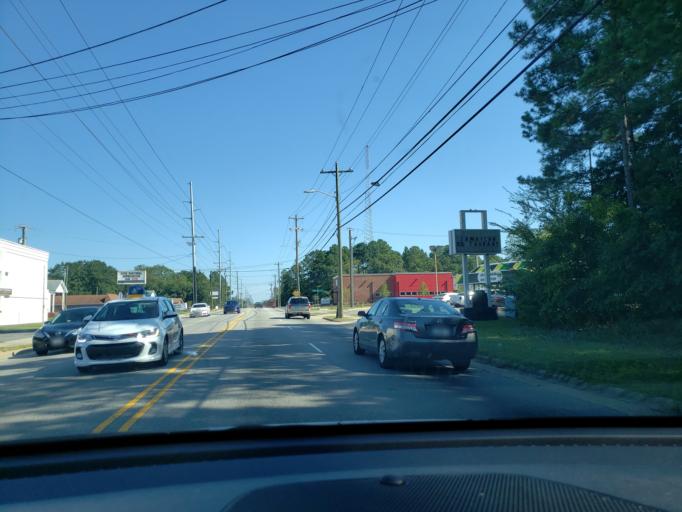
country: US
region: North Carolina
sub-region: Cumberland County
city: Fayetteville
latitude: 35.0878
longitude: -78.9077
